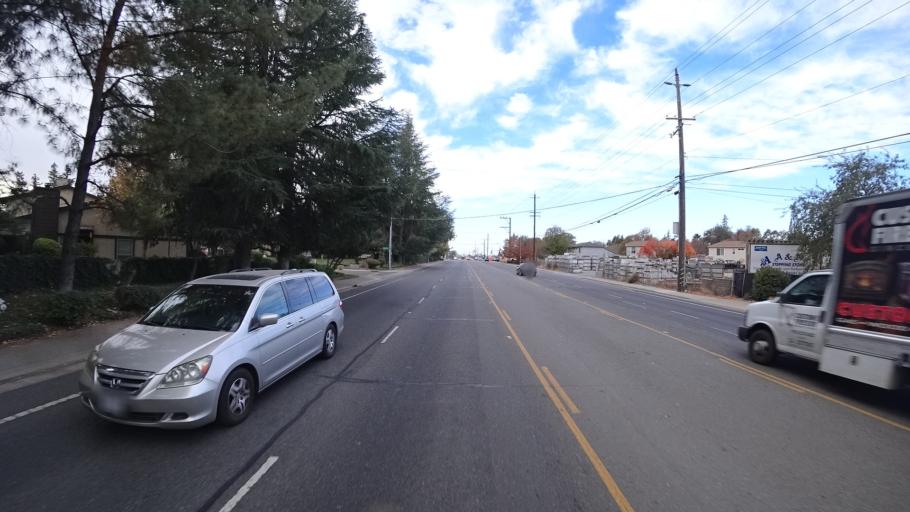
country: US
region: California
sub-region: Sacramento County
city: Antelope
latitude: 38.6816
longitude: -121.3166
